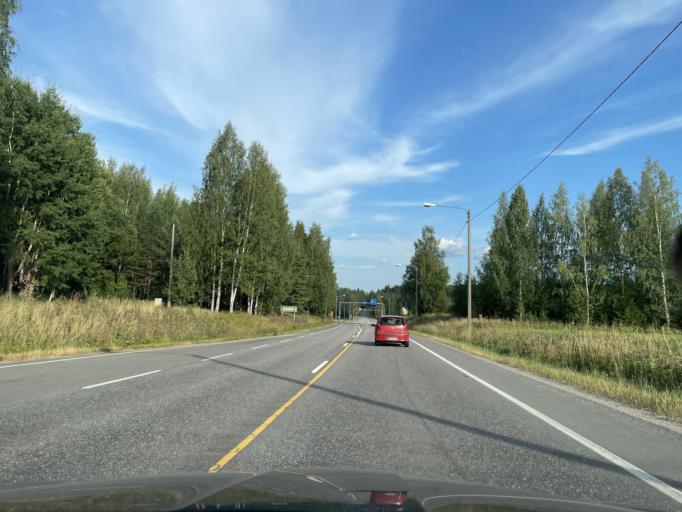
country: FI
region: Paijanne Tavastia
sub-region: Lahti
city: Padasjoki
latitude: 61.3448
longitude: 25.2423
